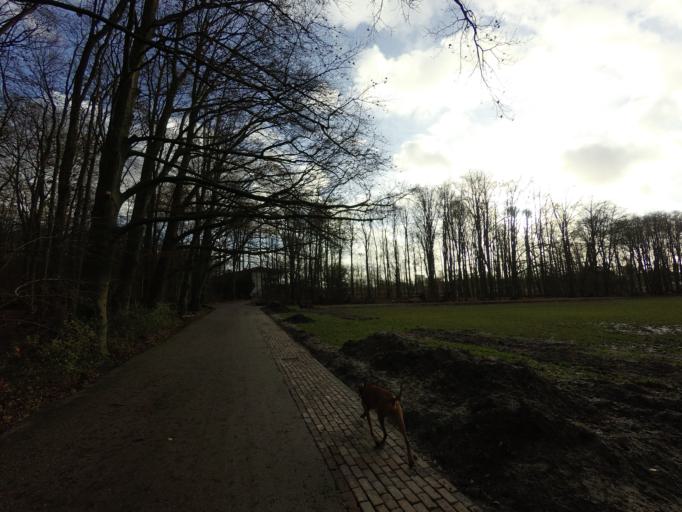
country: NL
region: South Holland
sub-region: Gemeente Rotterdam
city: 's-Gravenland
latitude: 51.9287
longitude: 4.5236
